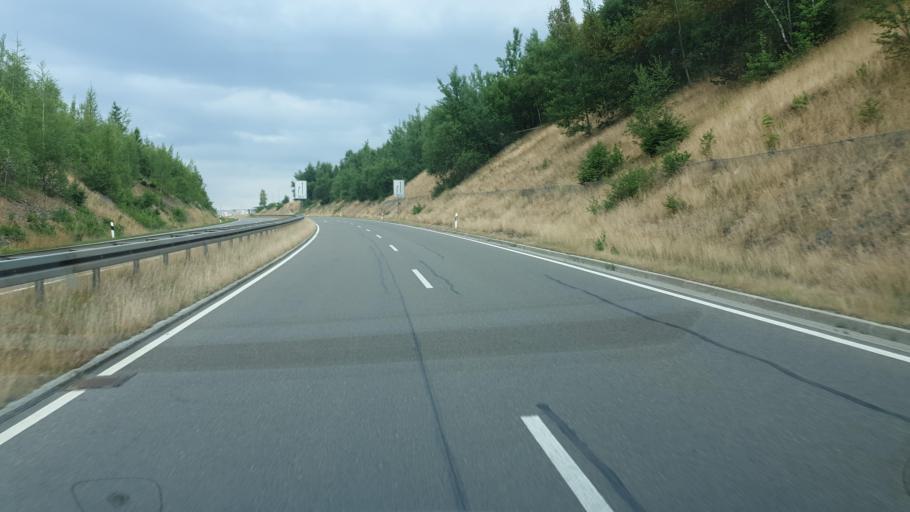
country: DE
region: Saxony
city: Reichenbach/Vogtland
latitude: 50.6061
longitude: 12.3162
